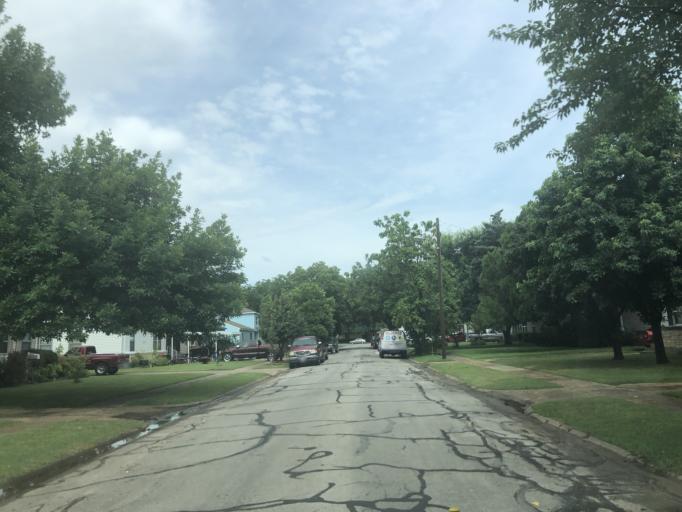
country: US
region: Texas
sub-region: Dallas County
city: Irving
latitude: 32.8020
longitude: -96.9502
